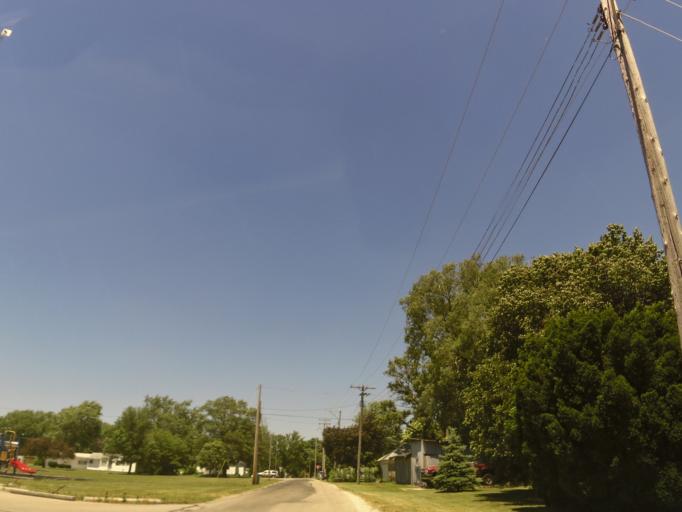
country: US
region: Illinois
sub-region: Livingston County
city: Chatsworth
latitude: 40.7532
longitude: -88.1865
